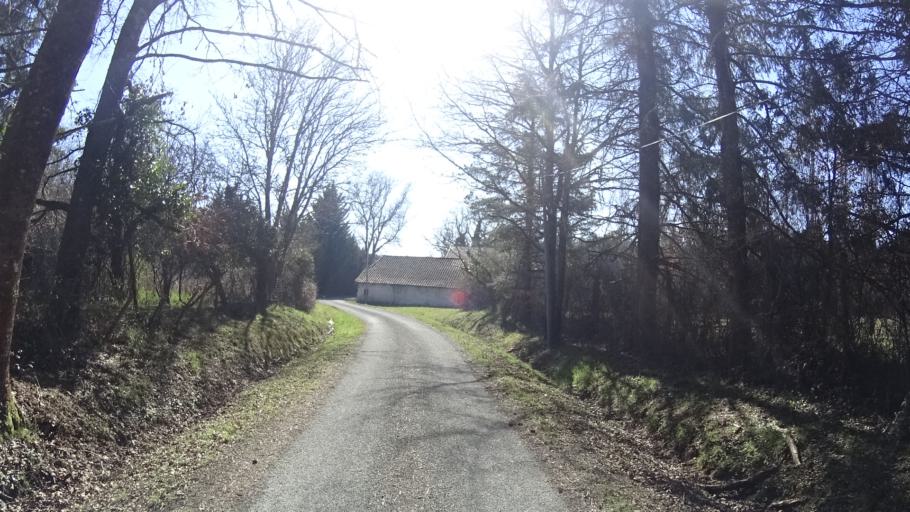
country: FR
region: Aquitaine
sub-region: Departement de la Dordogne
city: Saint-Aulaye
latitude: 45.1439
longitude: 0.2087
